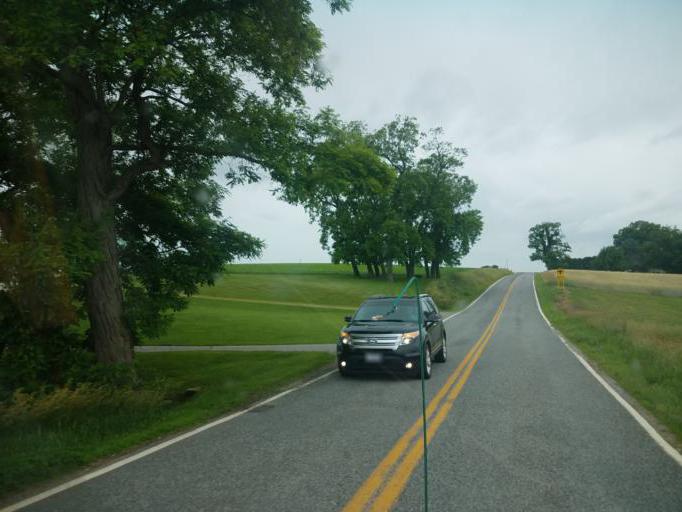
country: US
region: Ohio
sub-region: Columbiana County
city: Salem
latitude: 40.8212
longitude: -80.8363
